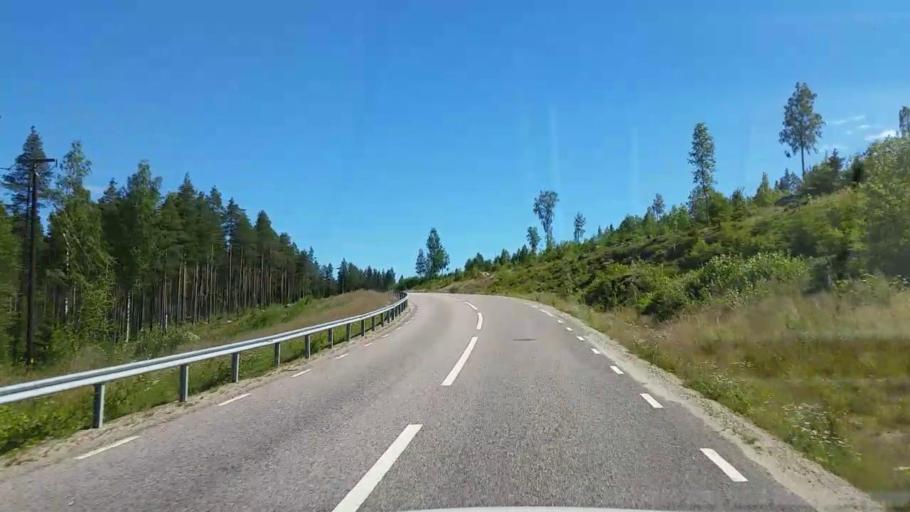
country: SE
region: Gaevleborg
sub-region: Ovanakers Kommun
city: Edsbyn
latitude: 61.5825
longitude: 15.6515
